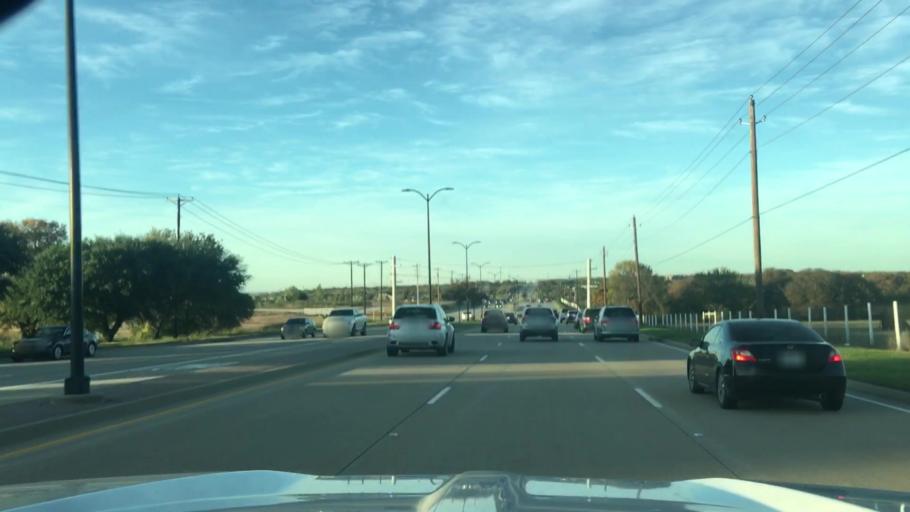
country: US
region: Texas
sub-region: Collin County
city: Frisco
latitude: 33.1689
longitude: -96.8030
